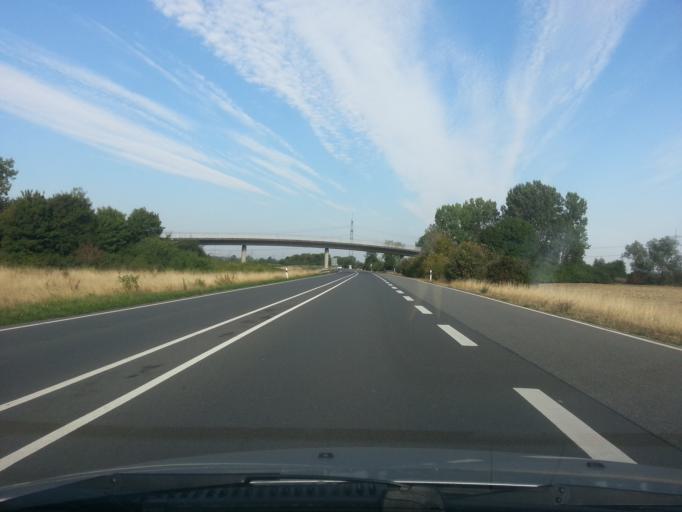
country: DE
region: Hesse
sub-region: Regierungsbezirk Darmstadt
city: Burstadt
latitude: 49.6369
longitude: 8.4421
